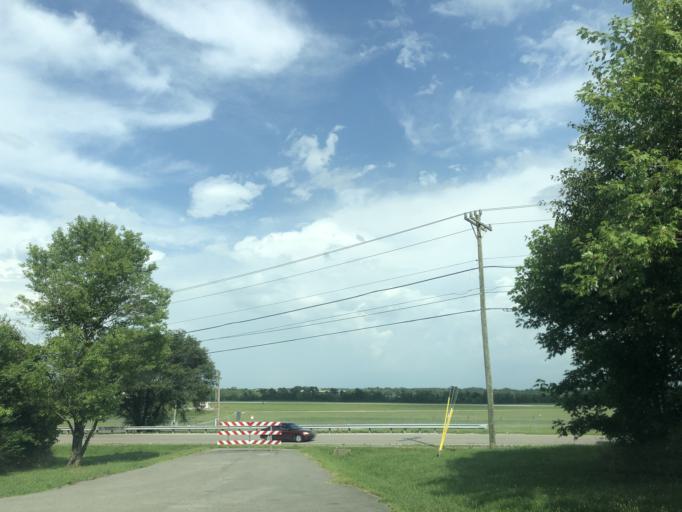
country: US
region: Tennessee
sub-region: Davidson County
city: Oak Hill
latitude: 36.1063
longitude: -86.6910
